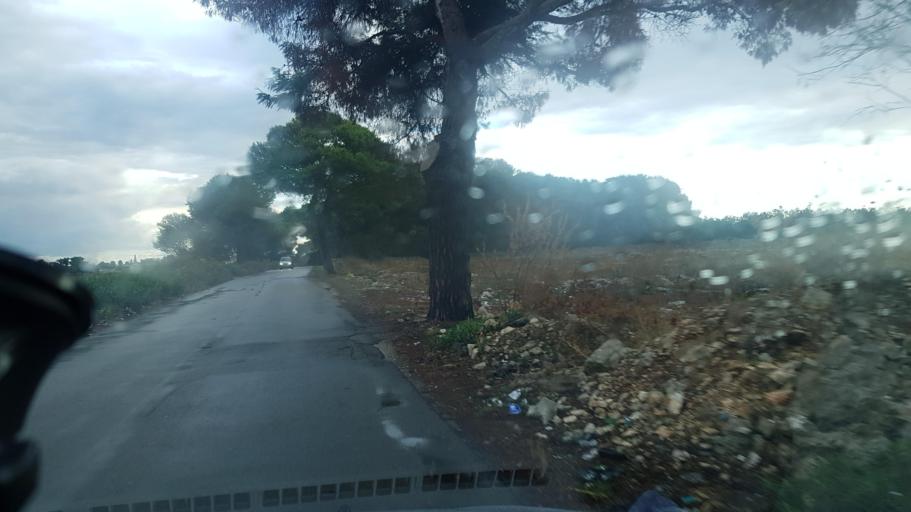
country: IT
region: Apulia
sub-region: Provincia di Lecce
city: Giorgilorio
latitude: 40.3820
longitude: 18.1465
